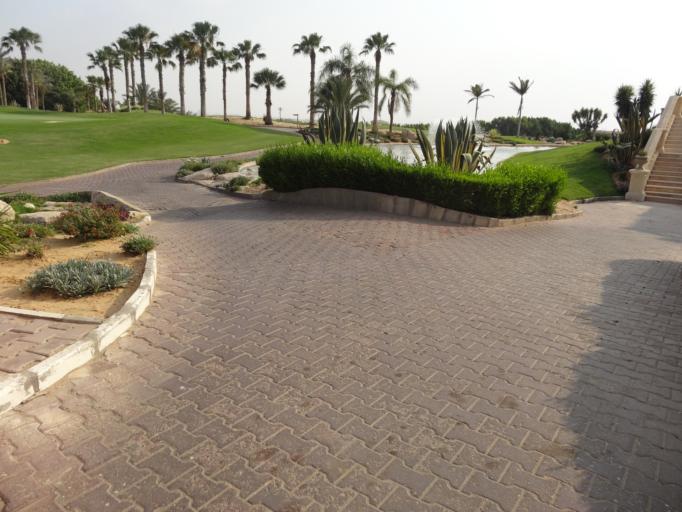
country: EG
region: Muhafazat al Qalyubiyah
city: Al Khankah
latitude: 30.0696
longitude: 31.4350
